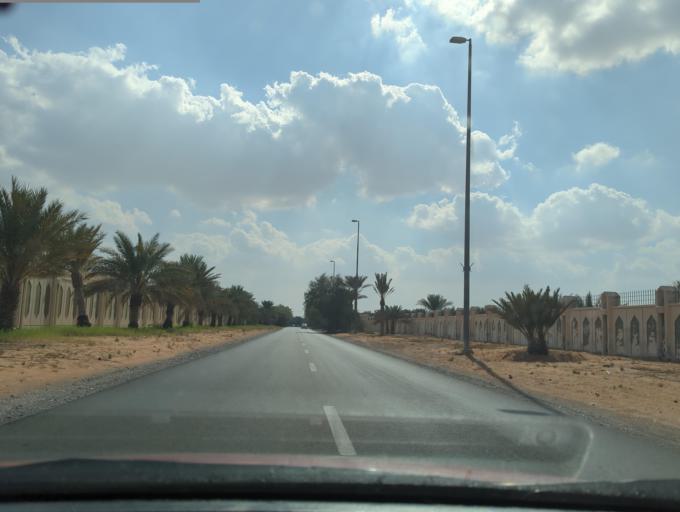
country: AE
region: Abu Dhabi
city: Al Ain
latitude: 24.1720
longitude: 55.6504
